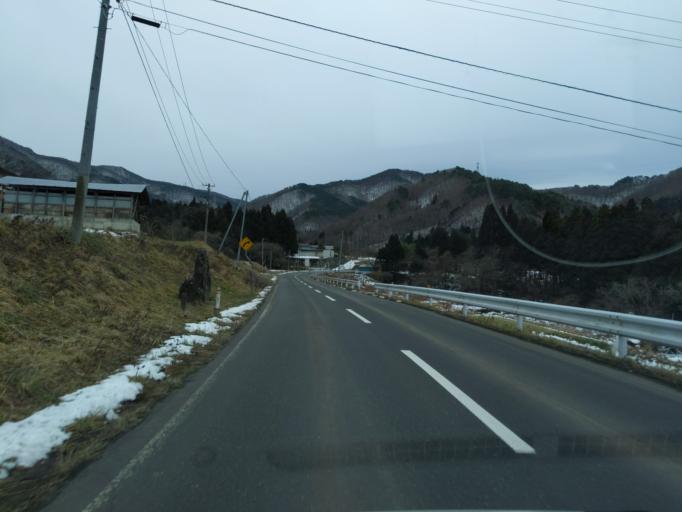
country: JP
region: Iwate
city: Mizusawa
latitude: 39.1068
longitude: 141.2727
